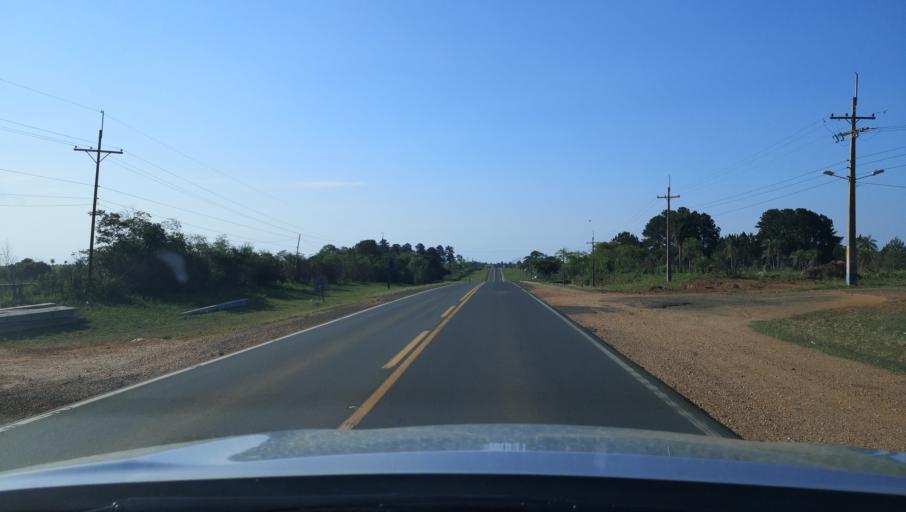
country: PY
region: Misiones
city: Santa Maria
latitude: -26.8532
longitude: -57.0359
